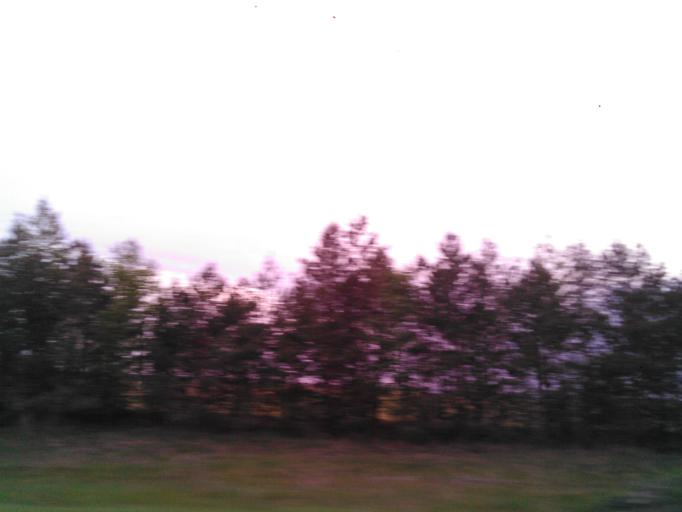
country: RU
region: Tatarstan
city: Russkiy Aktash
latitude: 55.0510
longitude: 52.0962
